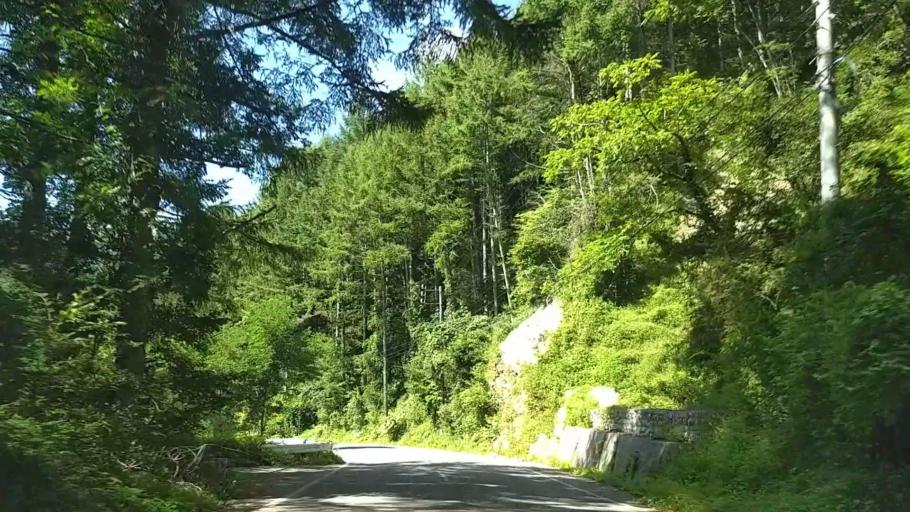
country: JP
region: Nagano
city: Matsumoto
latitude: 36.2050
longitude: 138.0891
